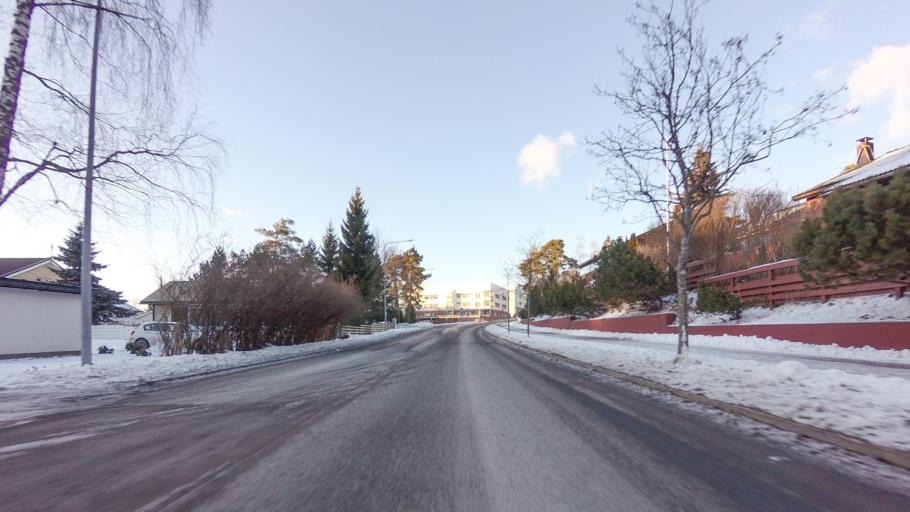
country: FI
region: Uusimaa
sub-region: Helsinki
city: Helsinki
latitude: 60.1640
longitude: 25.0471
